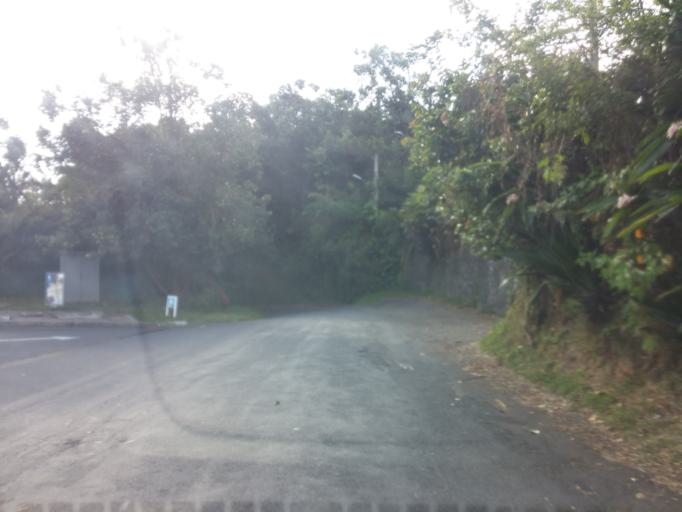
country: RE
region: Reunion
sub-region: Reunion
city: Saint-Denis
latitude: -20.8884
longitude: 55.4308
